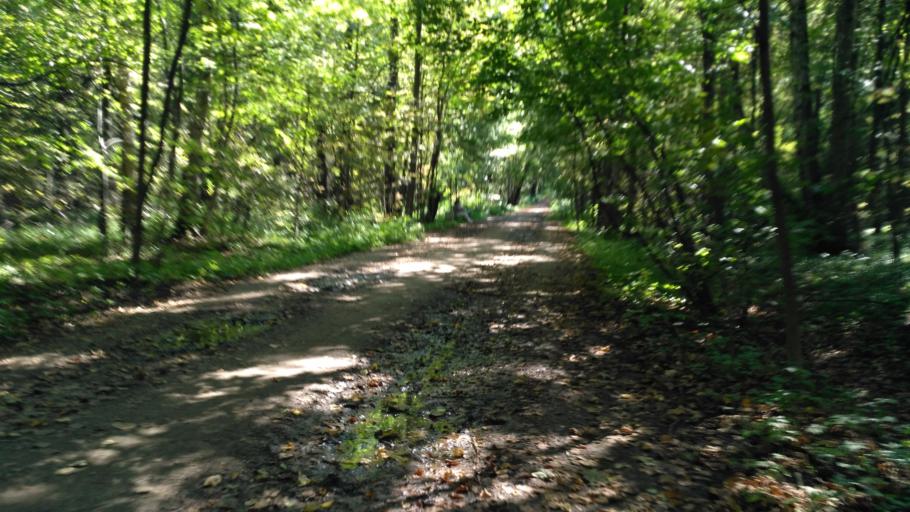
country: RU
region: Moscow
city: Ryazanskiy
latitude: 55.7730
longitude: 37.7592
